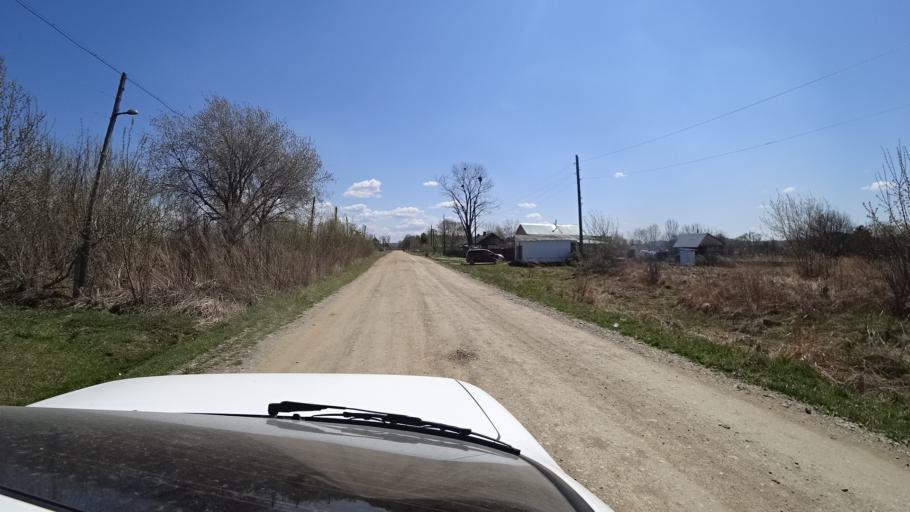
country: RU
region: Primorskiy
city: Dal'nerechensk
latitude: 45.8001
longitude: 133.7660
